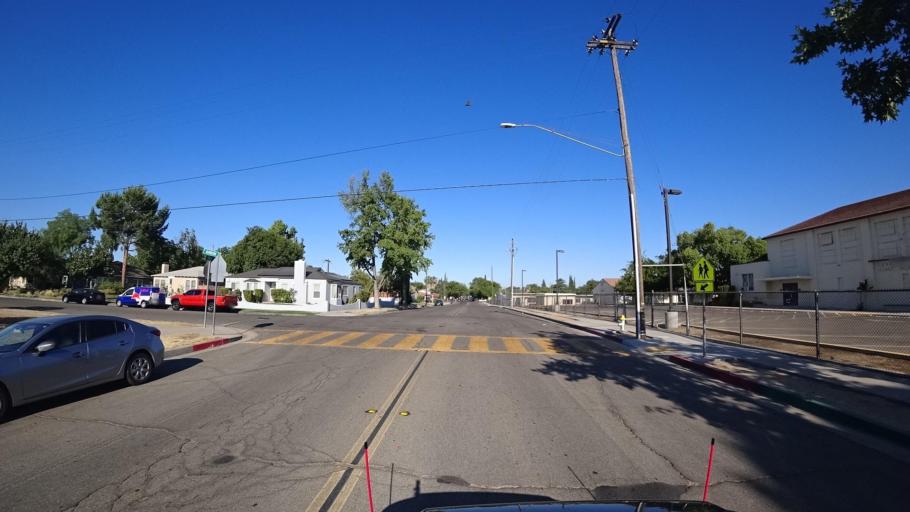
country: US
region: California
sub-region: Fresno County
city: Fresno
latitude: 36.7703
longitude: -119.8107
